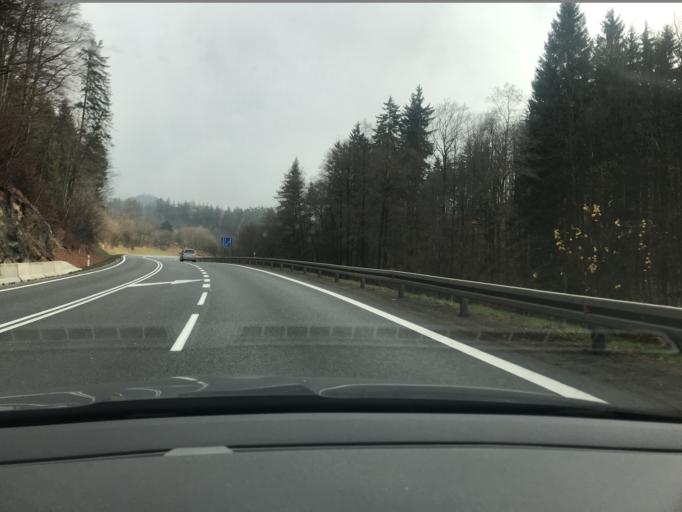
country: PL
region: Lower Silesian Voivodeship
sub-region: Powiat klodzki
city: Lewin Klodzki
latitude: 50.4071
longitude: 16.3295
